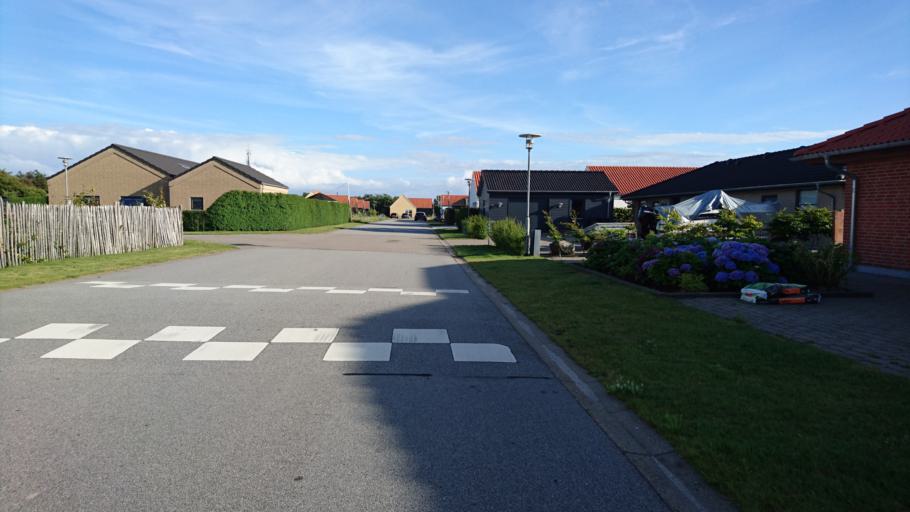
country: DK
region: North Denmark
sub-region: Frederikshavn Kommune
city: Skagen
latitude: 57.7334
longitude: 10.5913
